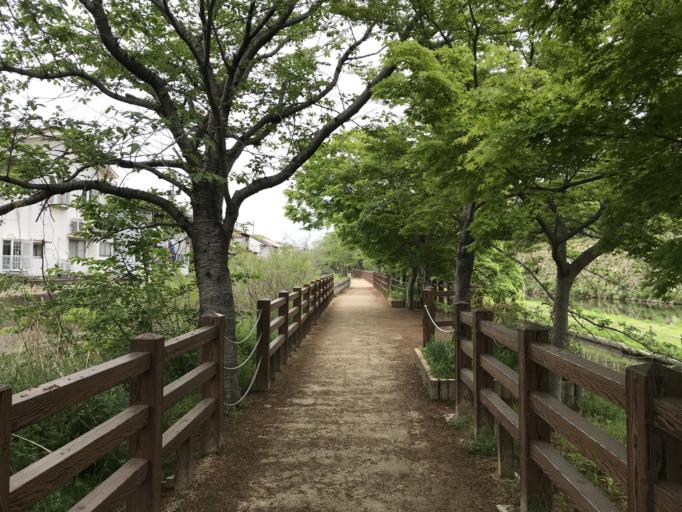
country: JP
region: Hyogo
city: Himeji
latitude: 34.8388
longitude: 134.6892
